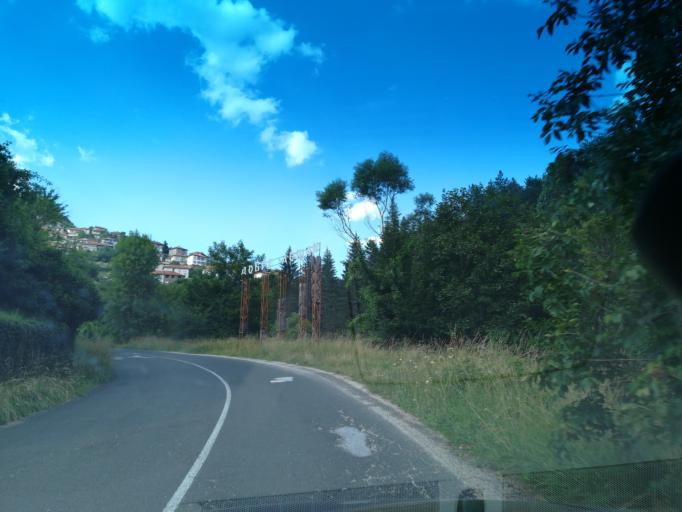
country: BG
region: Smolyan
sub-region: Obshtina Smolyan
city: Smolyan
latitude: 41.6522
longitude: 24.7722
